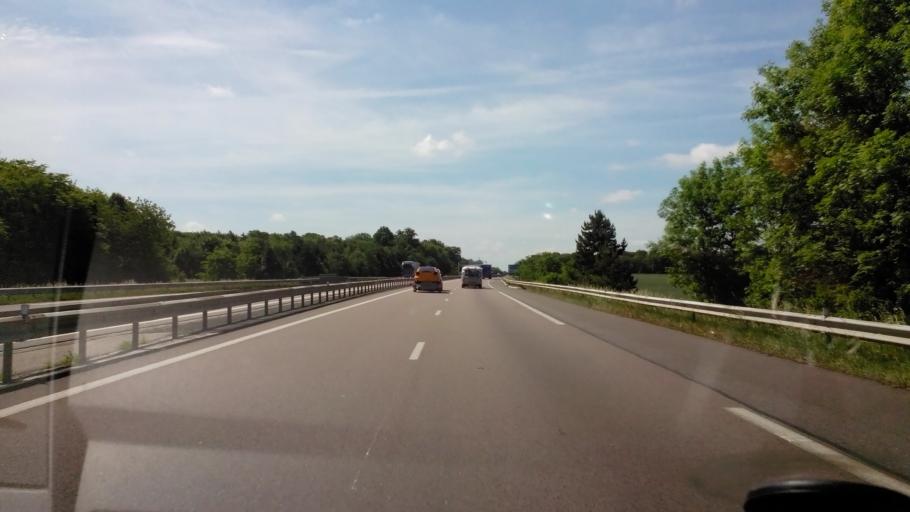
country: FR
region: Lorraine
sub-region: Departement de Meurthe-et-Moselle
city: Colombey-les-Belles
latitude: 48.5183
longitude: 5.9148
